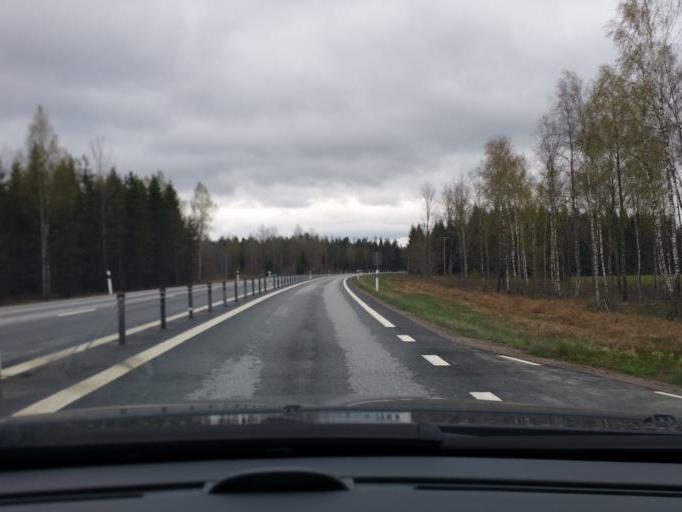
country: SE
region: Kronoberg
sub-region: Vaxjo Kommun
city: Vaexjoe
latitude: 56.9384
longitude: 14.7250
